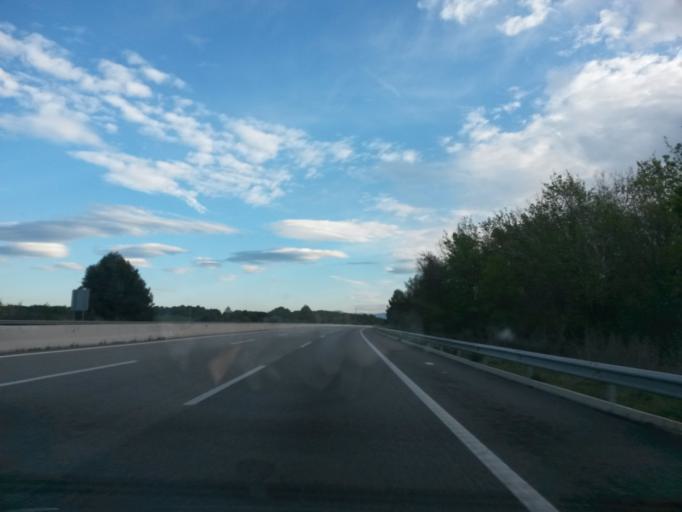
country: ES
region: Catalonia
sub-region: Provincia de Girona
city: Pontos
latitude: 42.1920
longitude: 2.9325
